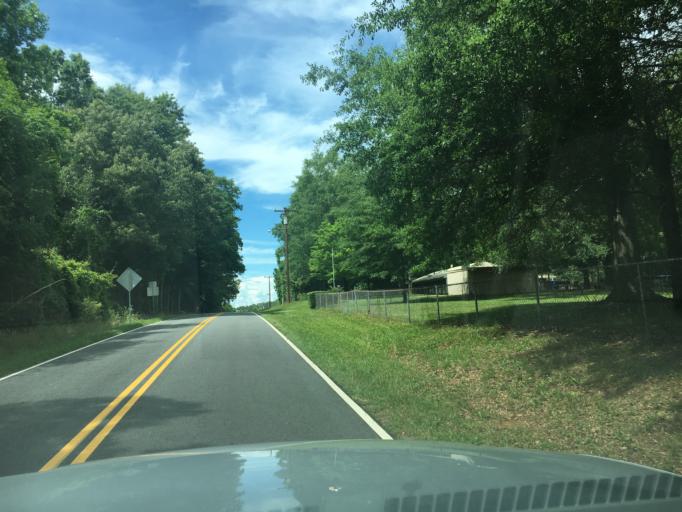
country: US
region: South Carolina
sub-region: Spartanburg County
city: Duncan
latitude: 34.8652
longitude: -82.1058
